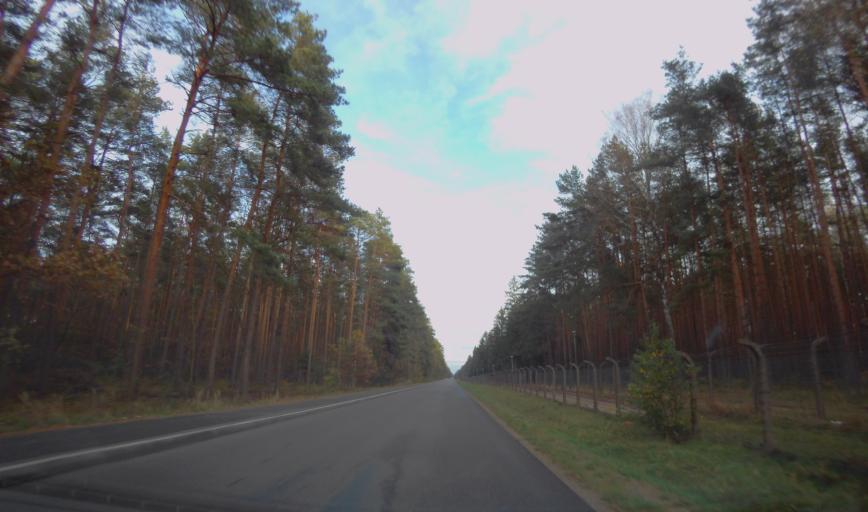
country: PL
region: Subcarpathian Voivodeship
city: Nowa Sarzyna
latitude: 50.3293
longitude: 22.2995
